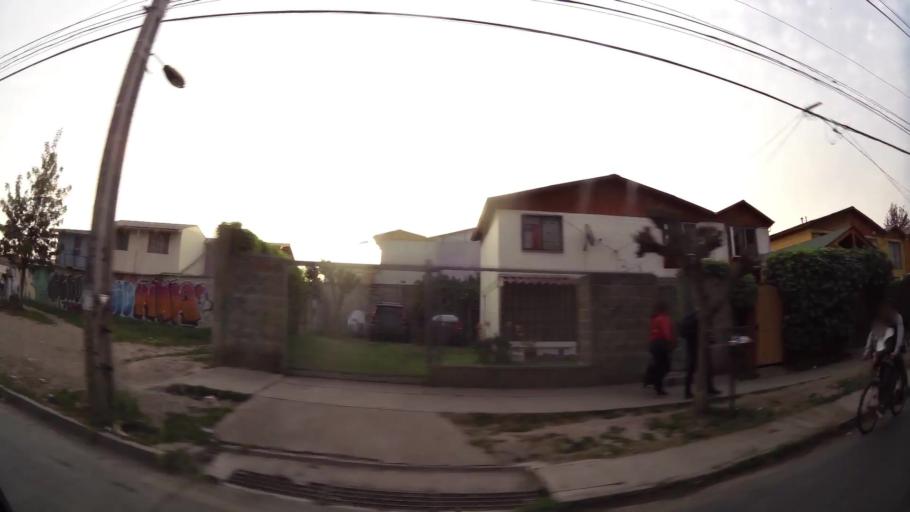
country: CL
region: Santiago Metropolitan
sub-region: Provincia de Santiago
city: Lo Prado
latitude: -33.5085
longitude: -70.7905
